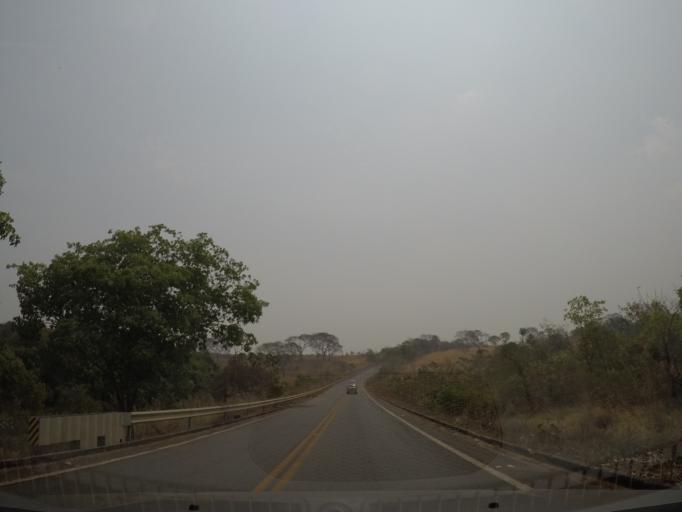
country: BR
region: Goias
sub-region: Pirenopolis
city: Pirenopolis
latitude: -15.8893
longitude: -48.8962
